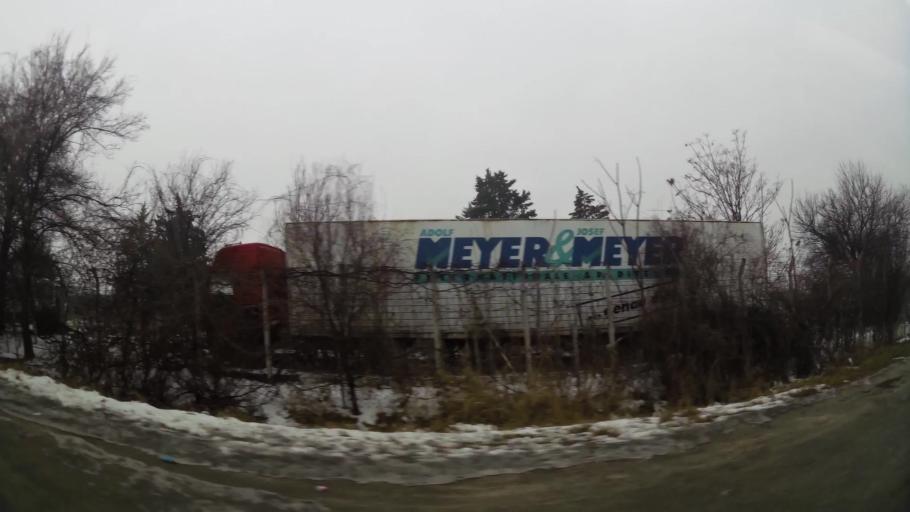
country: MK
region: Petrovec
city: Petrovec
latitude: 41.9504
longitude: 21.6308
